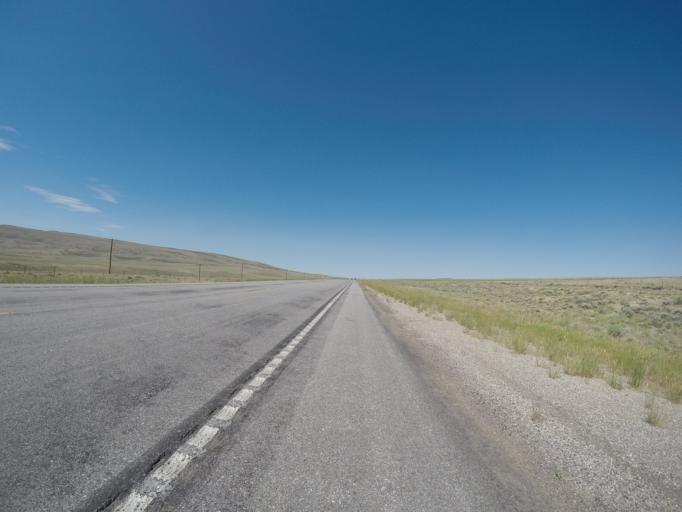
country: US
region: Wyoming
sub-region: Carbon County
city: Saratoga
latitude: 41.7991
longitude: -106.7143
